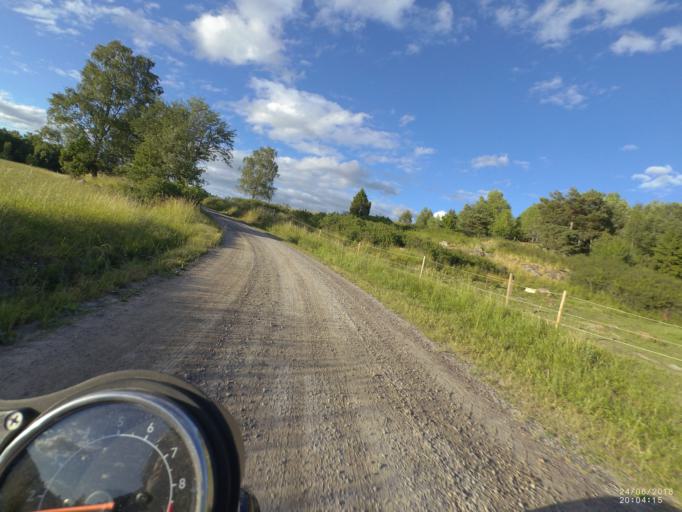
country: SE
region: Soedermanland
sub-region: Nykopings Kommun
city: Nykoping
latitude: 58.8020
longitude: 17.1279
